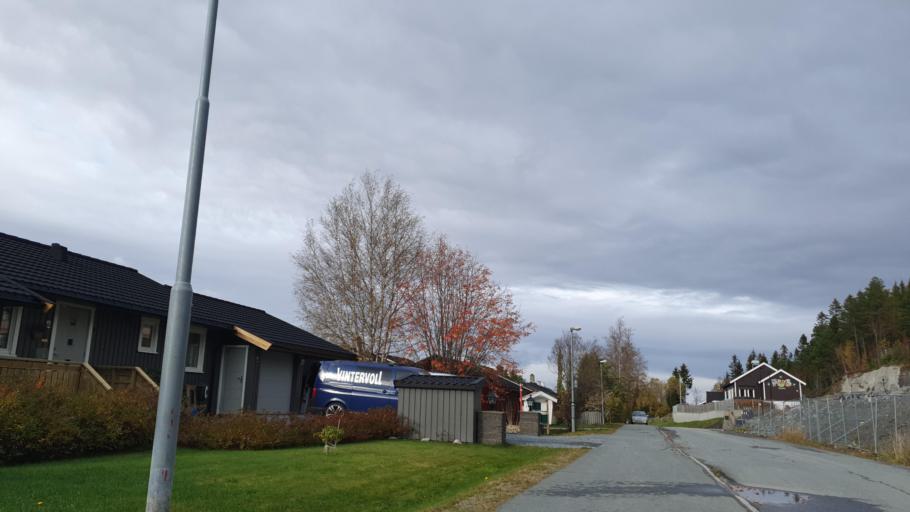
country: NO
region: Sor-Trondelag
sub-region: Klaebu
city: Klaebu
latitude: 63.3005
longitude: 10.4645
